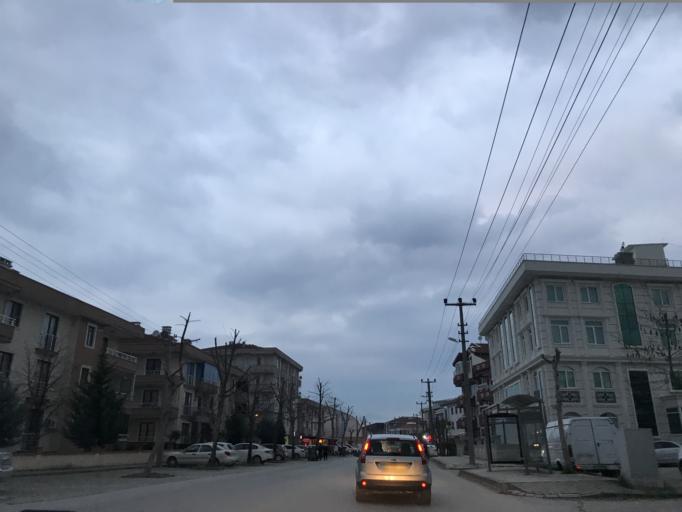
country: TR
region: Yalova
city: Yalova
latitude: 40.6473
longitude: 29.2604
